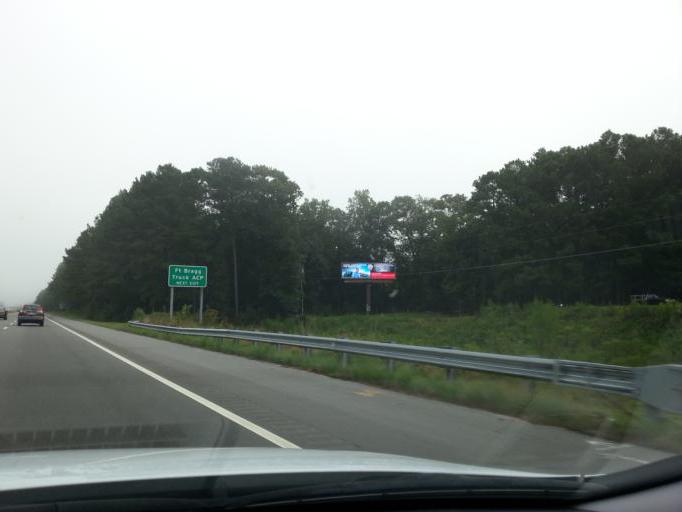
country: US
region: North Carolina
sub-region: Cumberland County
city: Fort Bragg
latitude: 35.0847
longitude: -78.9652
